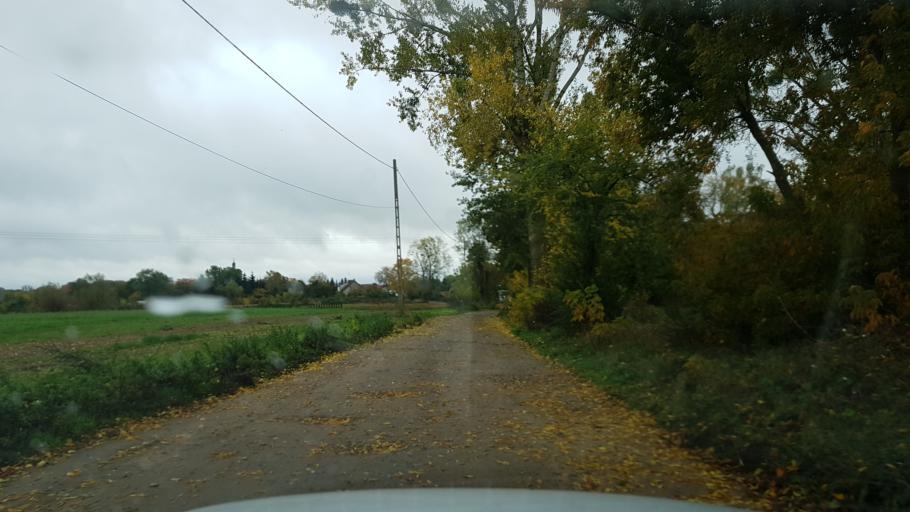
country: PL
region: West Pomeranian Voivodeship
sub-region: Powiat pyrzycki
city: Lipiany
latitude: 52.9713
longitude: 15.0110
